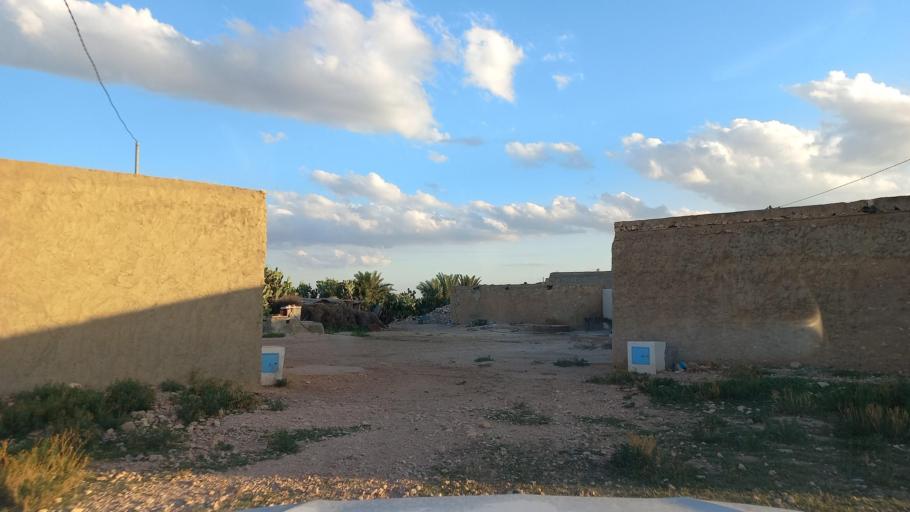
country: TN
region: Al Qasrayn
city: Sbiba
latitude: 35.3759
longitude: 9.0494
